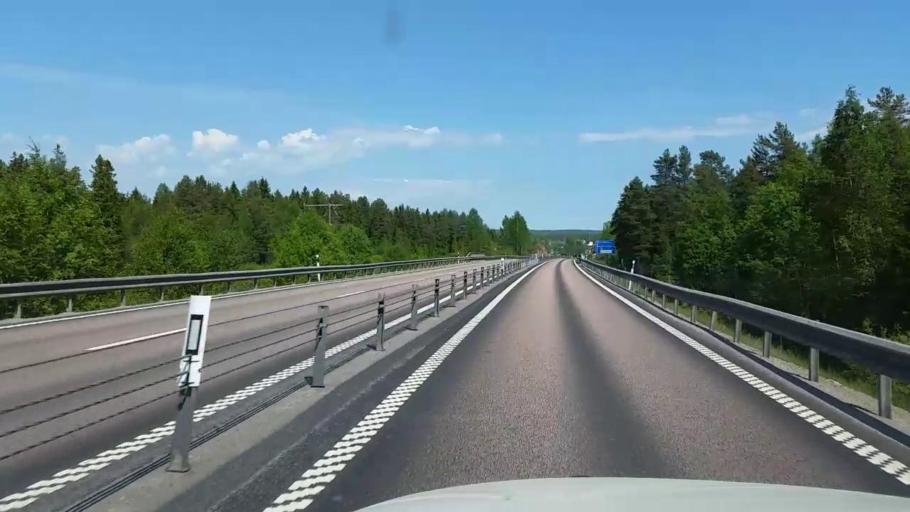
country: SE
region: Gaevleborg
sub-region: Hudiksvalls Kommun
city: Hudiksvall
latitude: 61.7383
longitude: 17.0711
